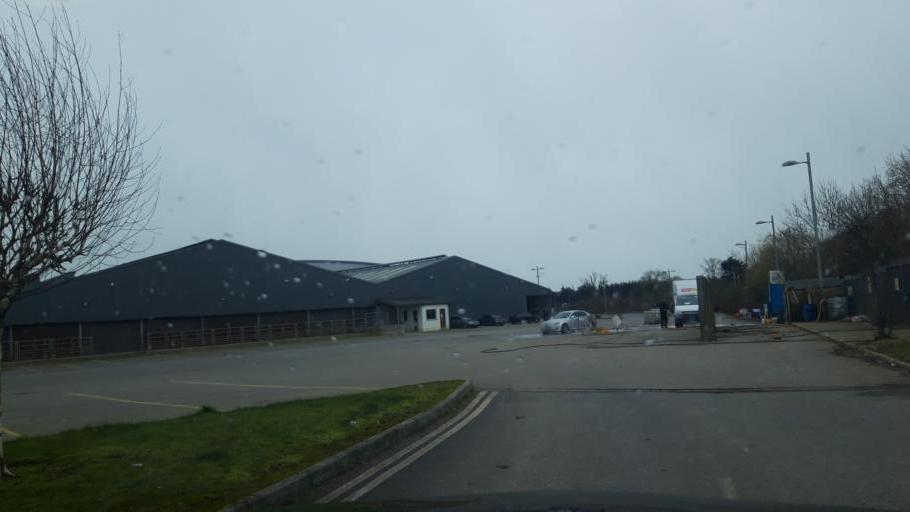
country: IE
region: Leinster
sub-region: Kilkenny
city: Kilkenny
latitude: 52.6522
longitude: -7.2120
